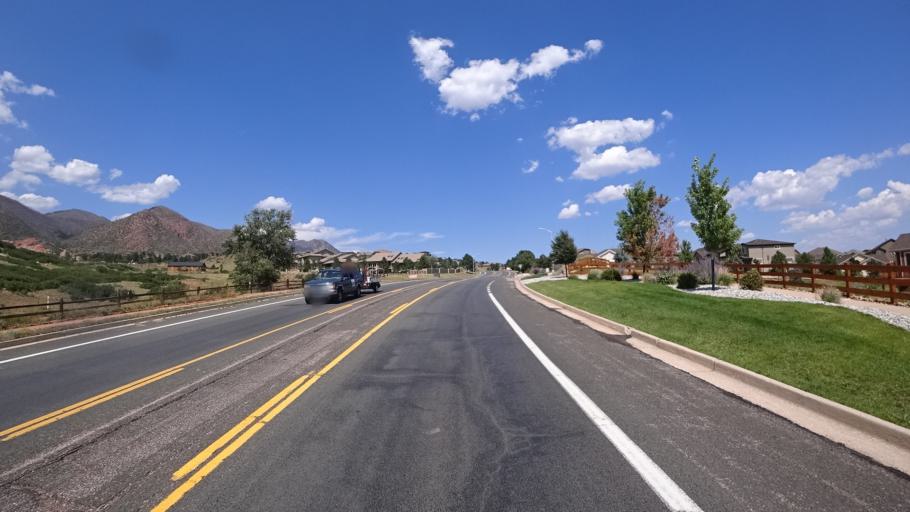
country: US
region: Colorado
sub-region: El Paso County
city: Manitou Springs
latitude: 38.9135
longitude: -104.8755
